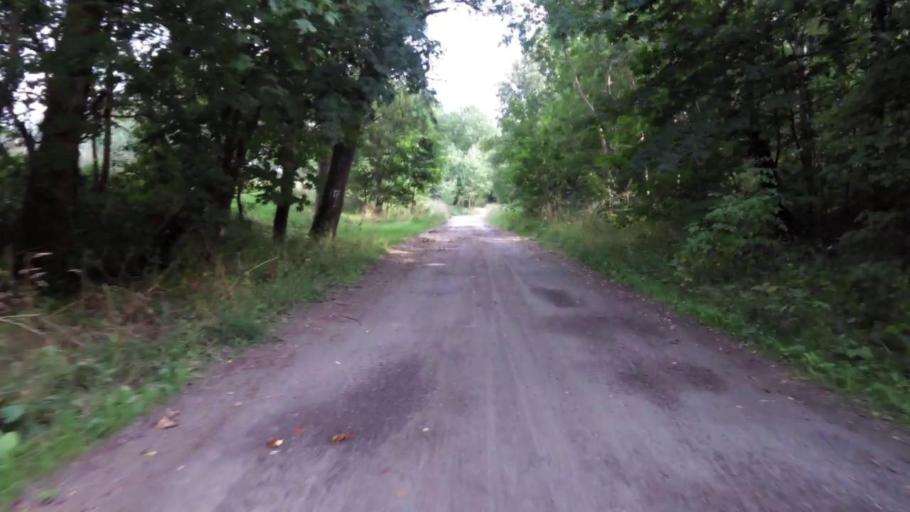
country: PL
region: West Pomeranian Voivodeship
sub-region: Powiat drawski
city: Drawsko Pomorskie
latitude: 53.5667
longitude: 15.8509
